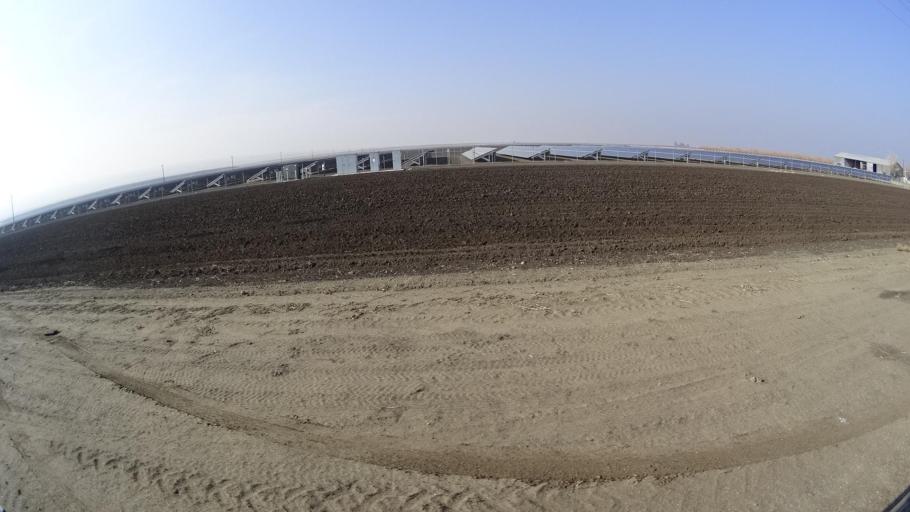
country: US
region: California
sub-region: Kern County
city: Buttonwillow
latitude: 35.3560
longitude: -119.4477
